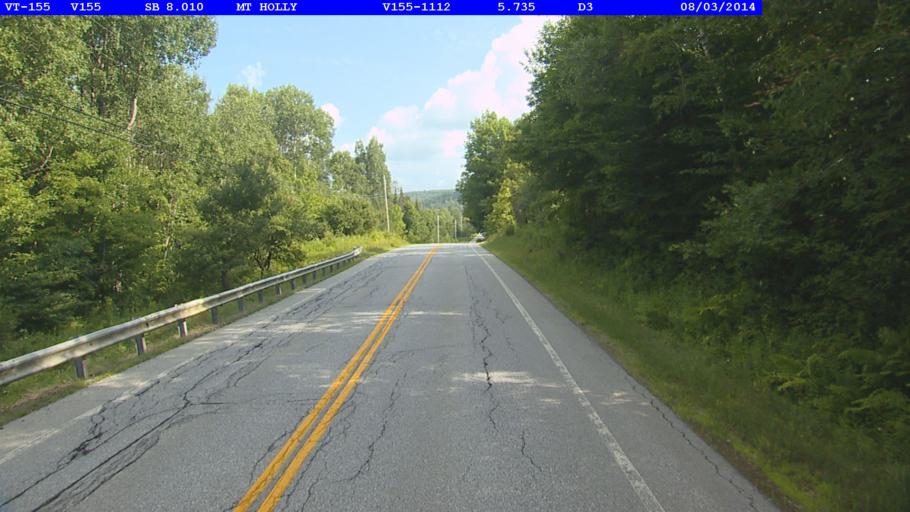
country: US
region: Vermont
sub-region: Rutland County
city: Rutland
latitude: 43.4255
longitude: -72.8571
